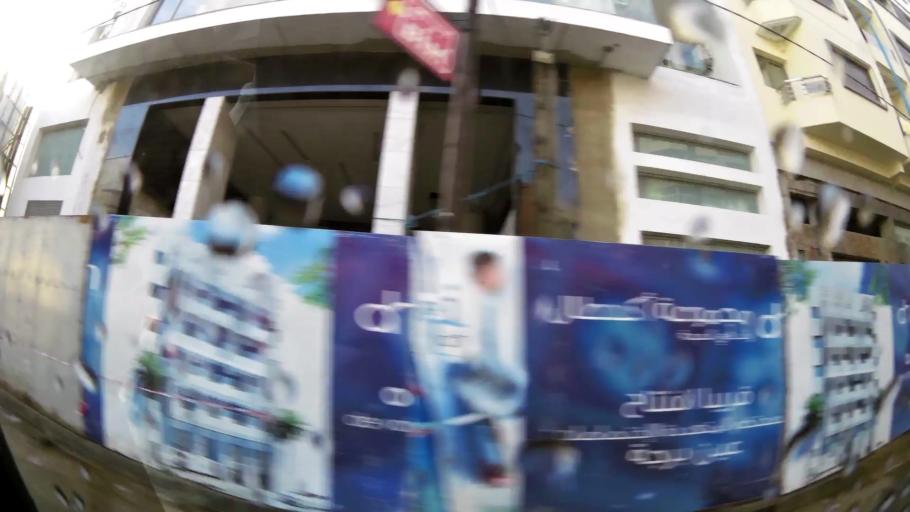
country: MA
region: Grand Casablanca
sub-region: Casablanca
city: Casablanca
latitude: 33.5853
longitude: -7.5966
